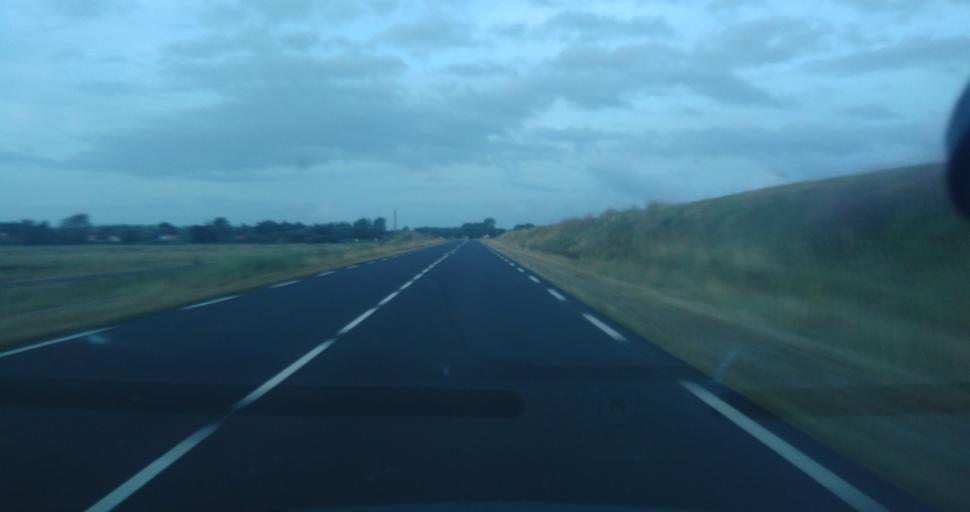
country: FR
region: Pays de la Loire
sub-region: Departement de la Vendee
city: Le Perrier
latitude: 46.7984
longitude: -1.9957
